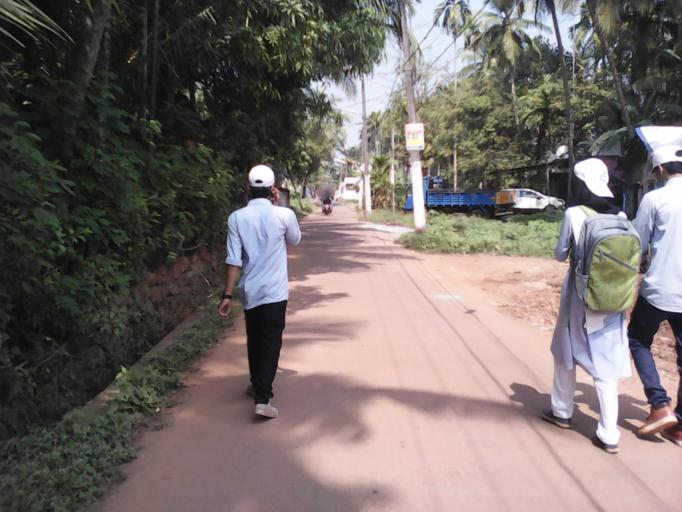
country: IN
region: Kerala
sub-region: Kozhikode
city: Kozhikode
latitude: 11.2840
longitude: 75.8241
